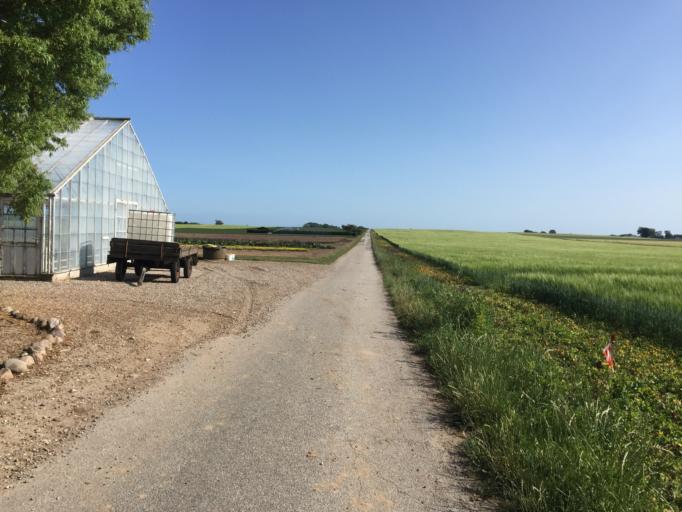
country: DK
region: Zealand
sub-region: Slagelse Kommune
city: Skaelskor
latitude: 55.2103
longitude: 11.1914
